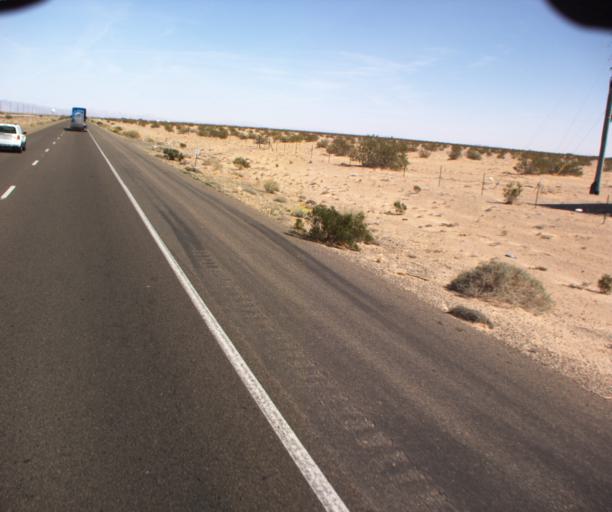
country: MX
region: Sonora
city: San Luis Rio Colorado
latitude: 32.4945
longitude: -114.6840
